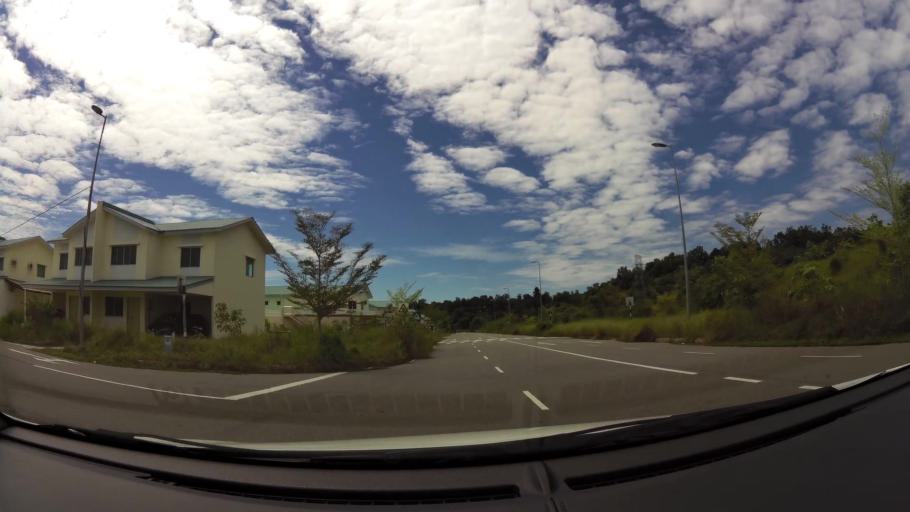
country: BN
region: Brunei and Muara
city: Bandar Seri Begawan
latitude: 4.9719
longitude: 115.0124
